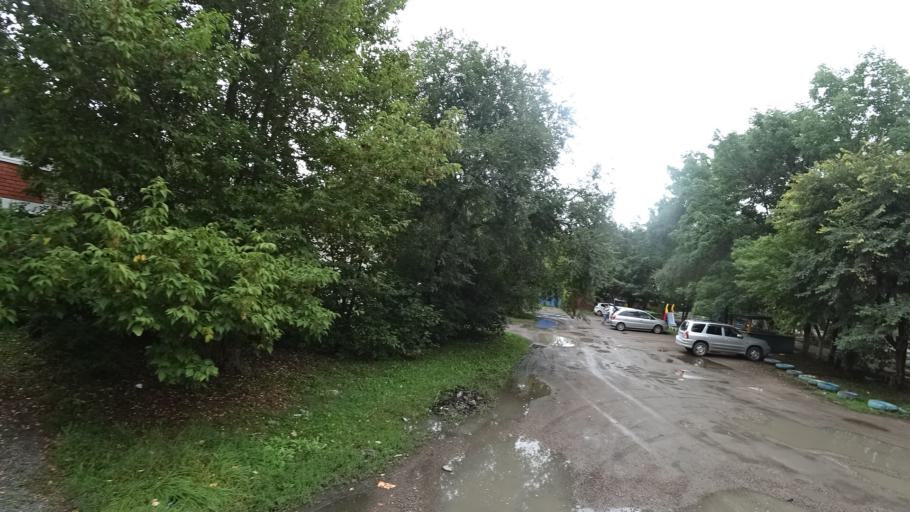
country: RU
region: Primorskiy
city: Chernigovka
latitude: 44.3422
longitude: 132.5787
